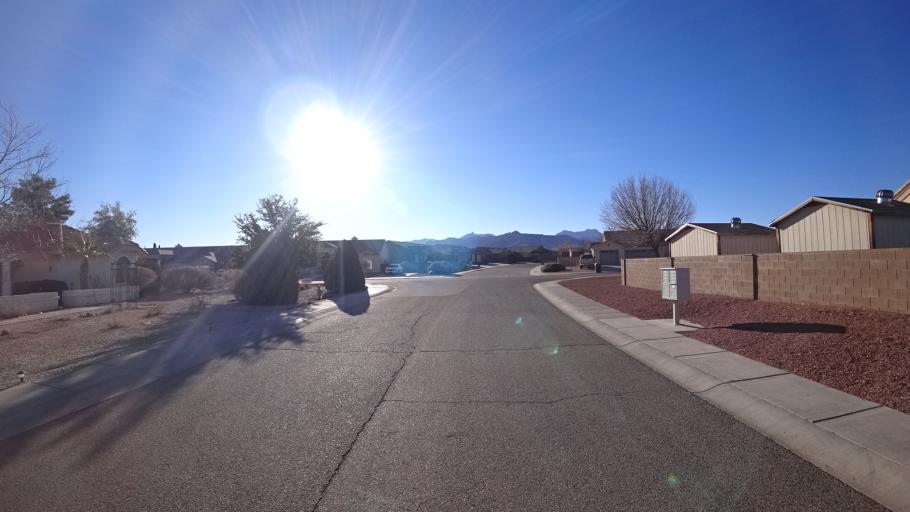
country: US
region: Arizona
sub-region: Mohave County
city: New Kingman-Butler
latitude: 35.2208
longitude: -113.9724
